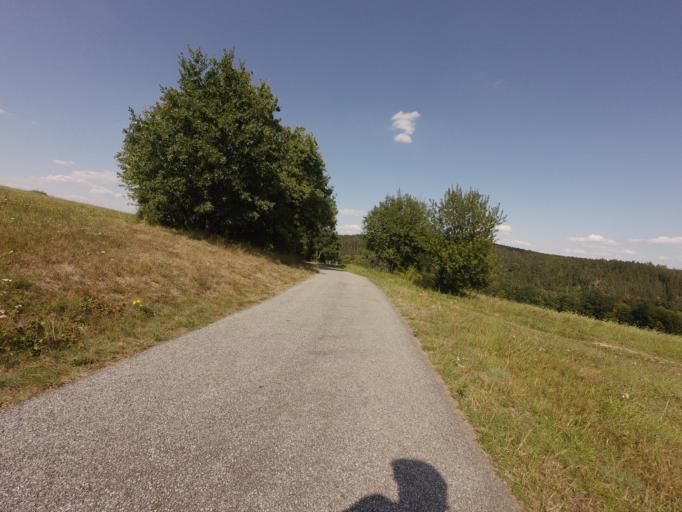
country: CZ
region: Jihocesky
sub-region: Okres Ceske Budejovice
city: Hluboka nad Vltavou
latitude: 49.1143
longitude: 14.4583
